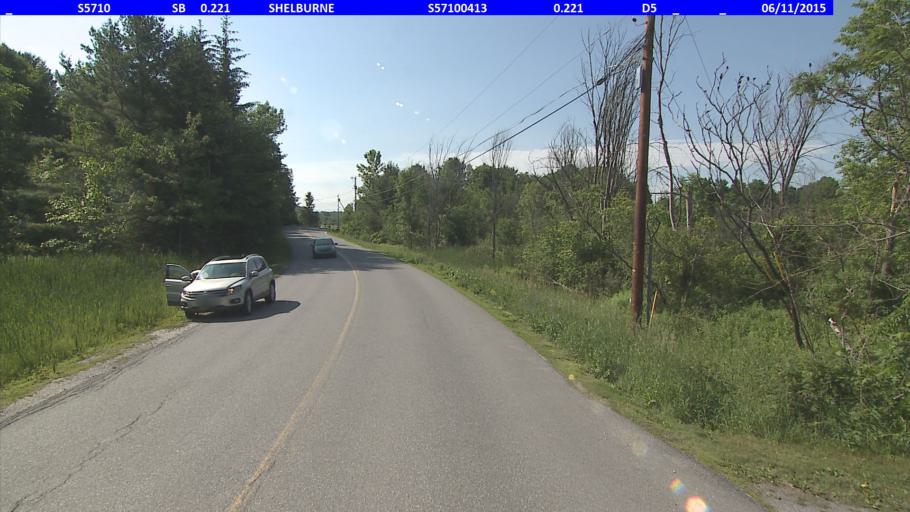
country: US
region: Vermont
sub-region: Chittenden County
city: Hinesburg
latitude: 44.3680
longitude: -73.1805
